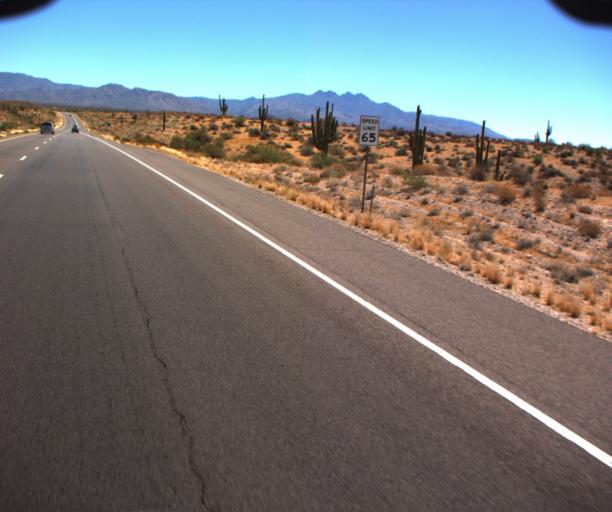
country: US
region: Arizona
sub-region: Maricopa County
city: Rio Verde
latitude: 33.6313
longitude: -111.5536
